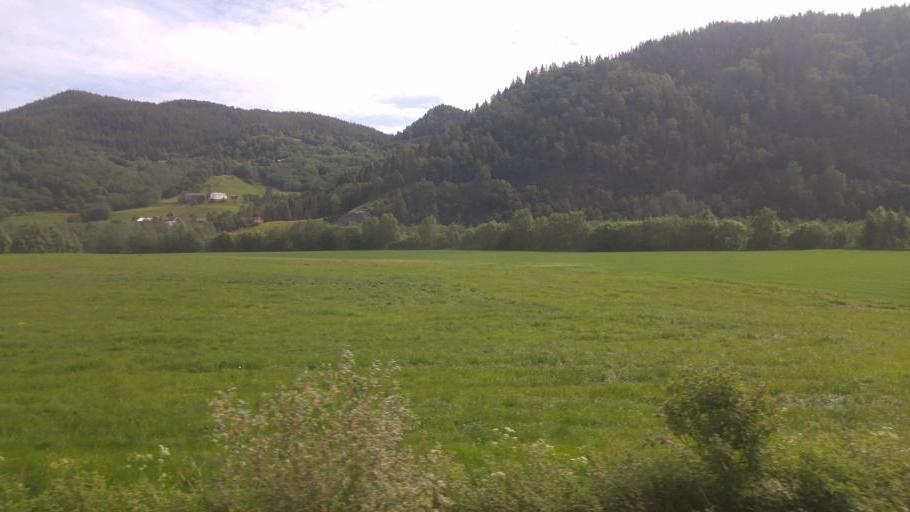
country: NO
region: Sor-Trondelag
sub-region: Midtre Gauldal
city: Storen
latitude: 63.0863
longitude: 10.2440
